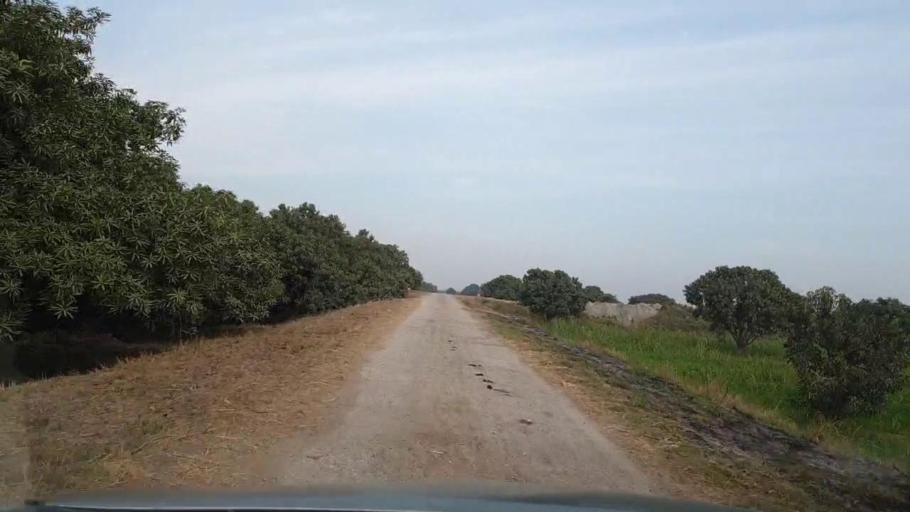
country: PK
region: Sindh
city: Matiari
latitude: 25.5580
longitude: 68.5410
